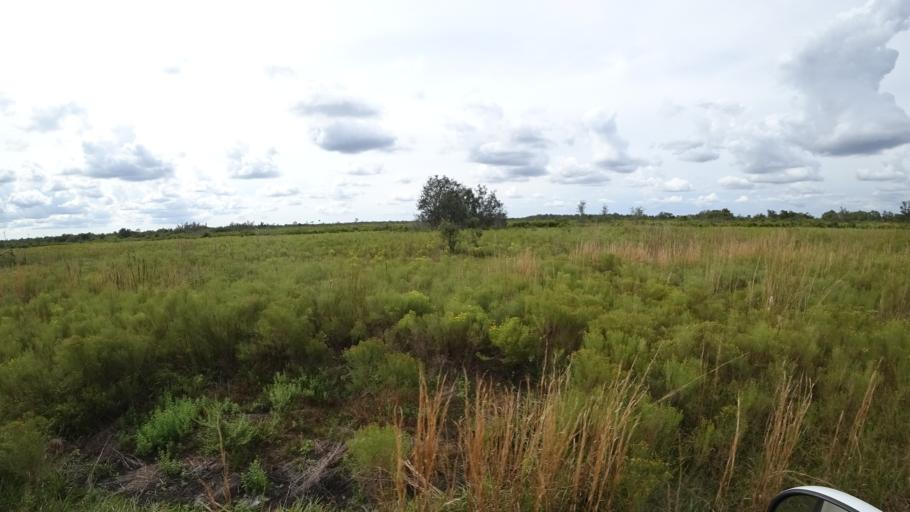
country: US
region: Florida
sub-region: Hillsborough County
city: Wimauma
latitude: 27.5464
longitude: -82.1358
